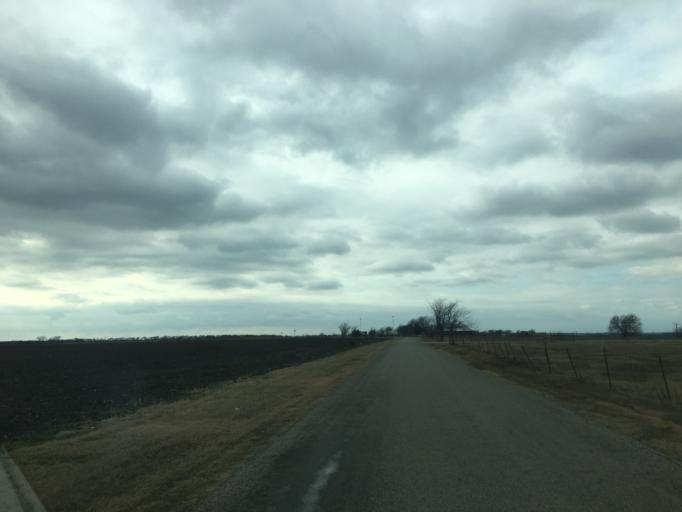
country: US
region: Texas
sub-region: Ellis County
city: Palmer
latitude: 32.4630
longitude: -96.6473
